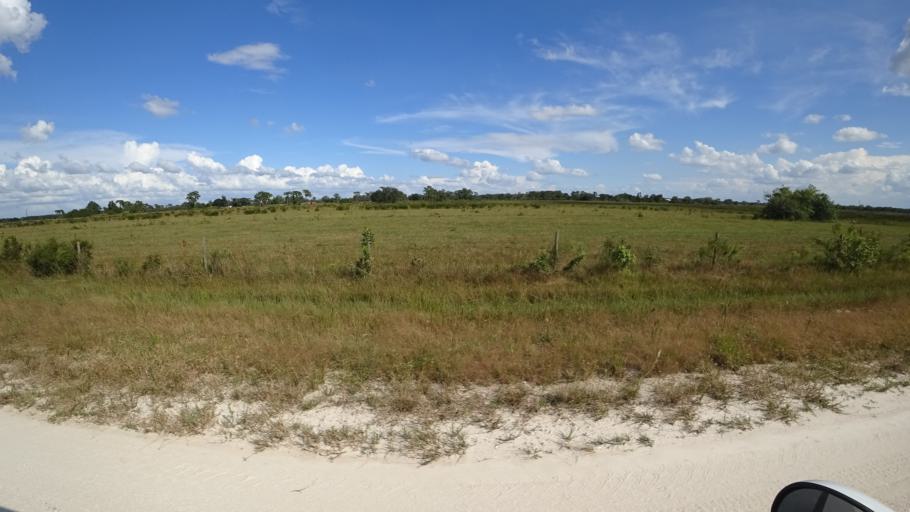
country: US
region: Florida
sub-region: DeSoto County
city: Arcadia
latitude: 27.3335
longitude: -82.0806
